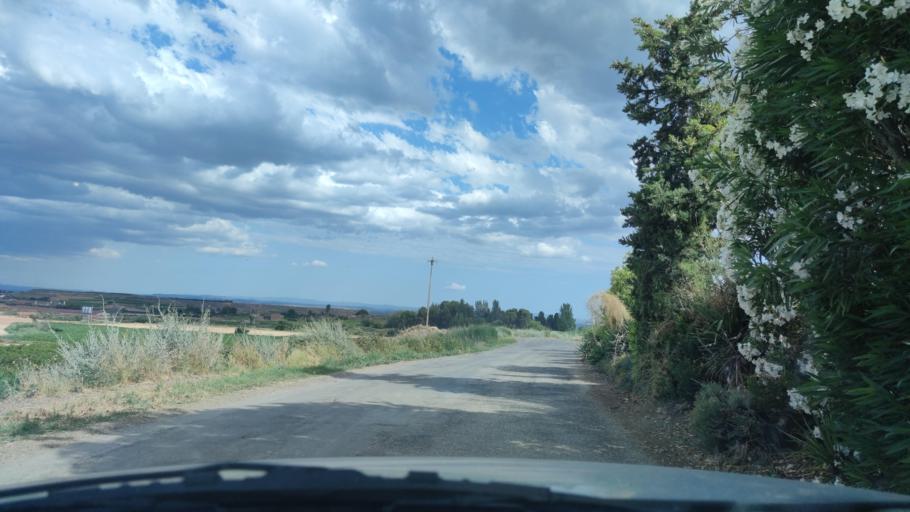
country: ES
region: Catalonia
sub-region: Provincia de Lleida
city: Alcarras
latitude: 41.6022
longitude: 0.5449
